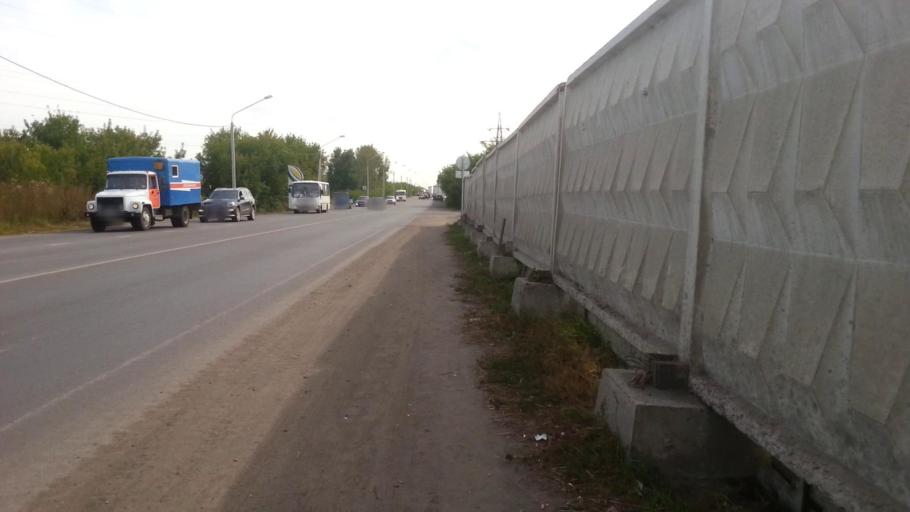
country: RU
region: Altai Krai
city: Novosilikatnyy
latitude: 53.3484
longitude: 83.6202
